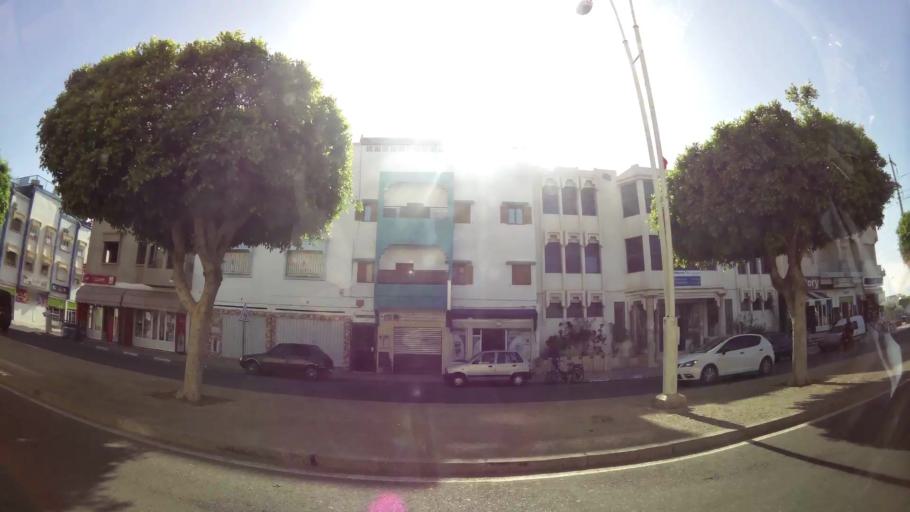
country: MA
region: Oued ed Dahab-Lagouira
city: Dakhla
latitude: 30.4133
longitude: -9.5686
